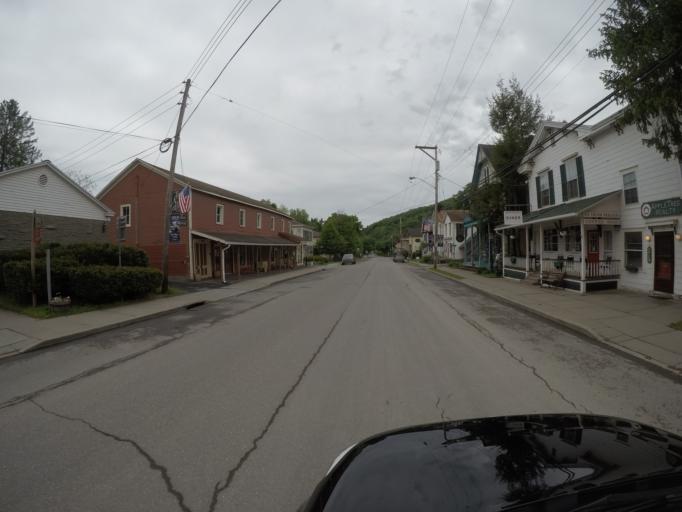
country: US
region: New York
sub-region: Delaware County
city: Delhi
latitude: 42.1897
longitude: -74.7842
